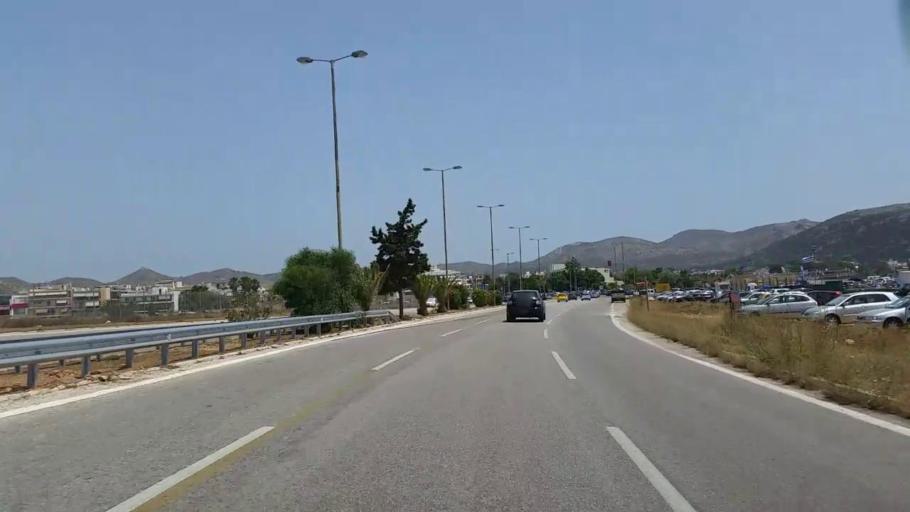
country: GR
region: Attica
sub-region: Nomarchia Anatolikis Attikis
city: Anavyssos
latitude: 37.7262
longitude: 23.9404
